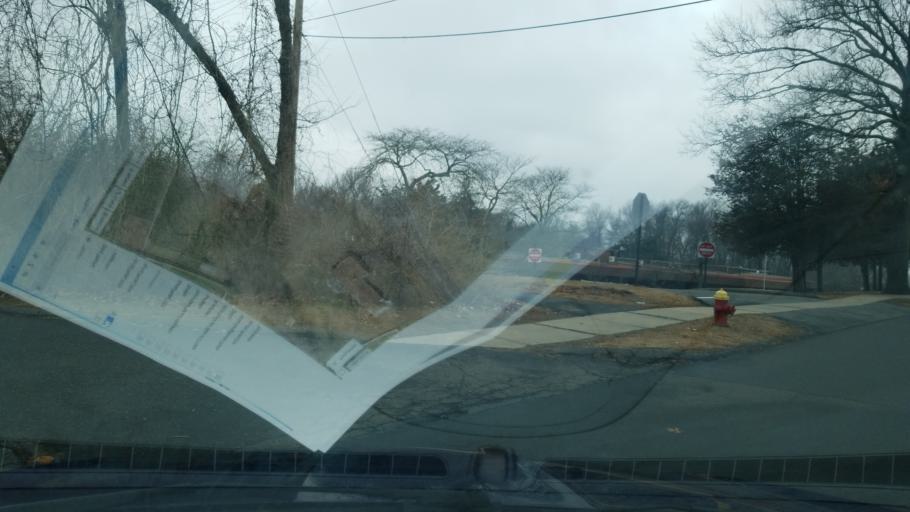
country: US
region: Connecticut
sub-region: Hartford County
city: Newington
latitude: 41.6784
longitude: -72.6827
